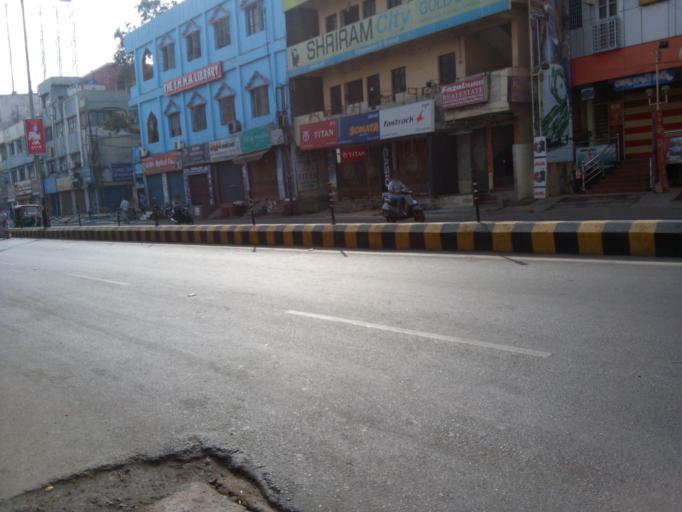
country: IN
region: Andhra Pradesh
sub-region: Krishna
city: Vijayawada
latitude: 16.5142
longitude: 80.6310
